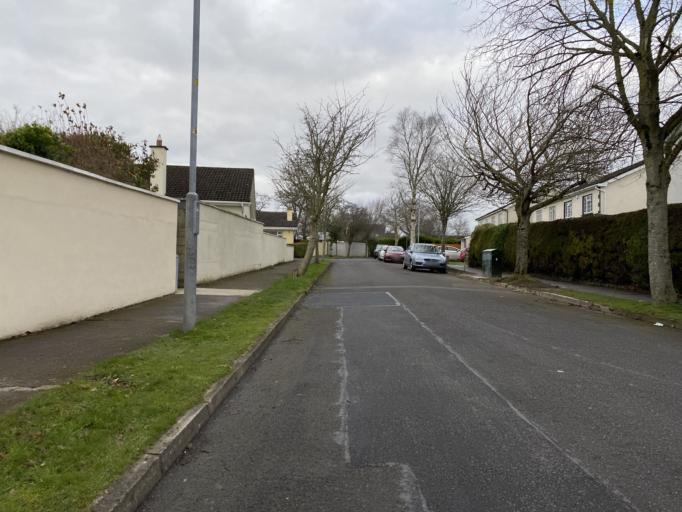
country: IE
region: Leinster
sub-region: Kildare
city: Celbridge
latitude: 53.3538
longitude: -6.5460
